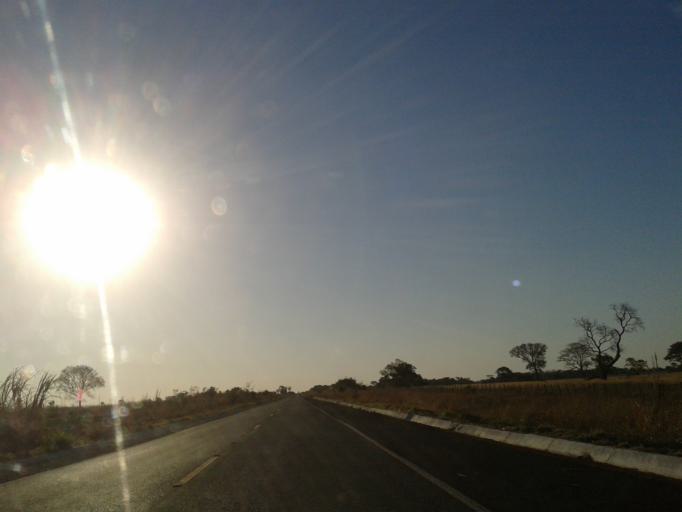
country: BR
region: Minas Gerais
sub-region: Santa Vitoria
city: Santa Vitoria
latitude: -19.1008
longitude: -50.3315
